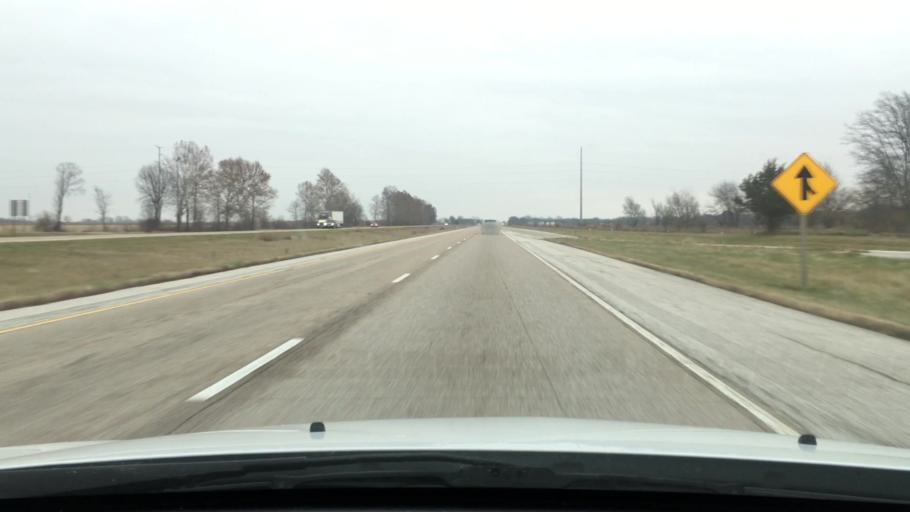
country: US
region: Illinois
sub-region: Scott County
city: Winchester
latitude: 39.6811
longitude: -90.4530
